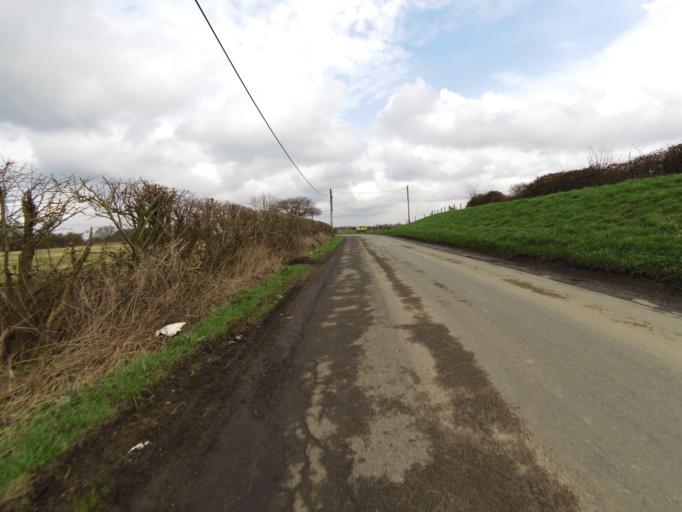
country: GB
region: England
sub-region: Doncaster
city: Moss
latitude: 53.5947
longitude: -1.0879
